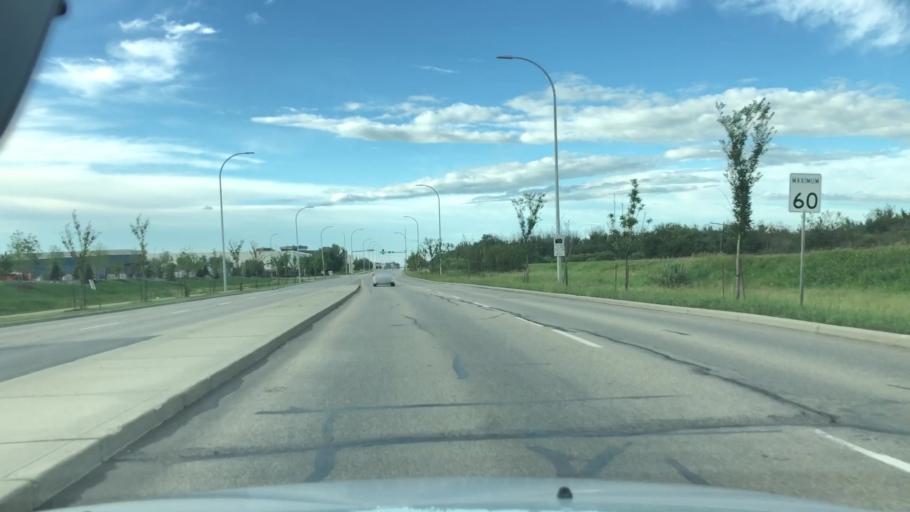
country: CA
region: Alberta
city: St. Albert
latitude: 53.6337
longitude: -113.5658
